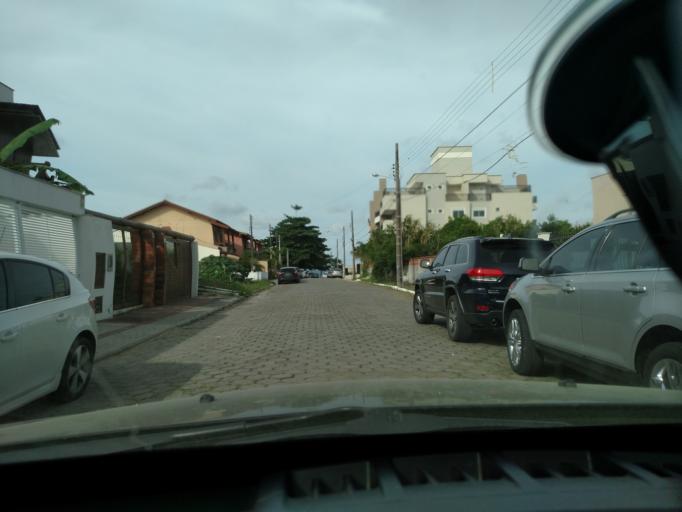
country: BR
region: Santa Catarina
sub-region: Porto Belo
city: Porto Belo
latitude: -27.1949
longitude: -48.4993
